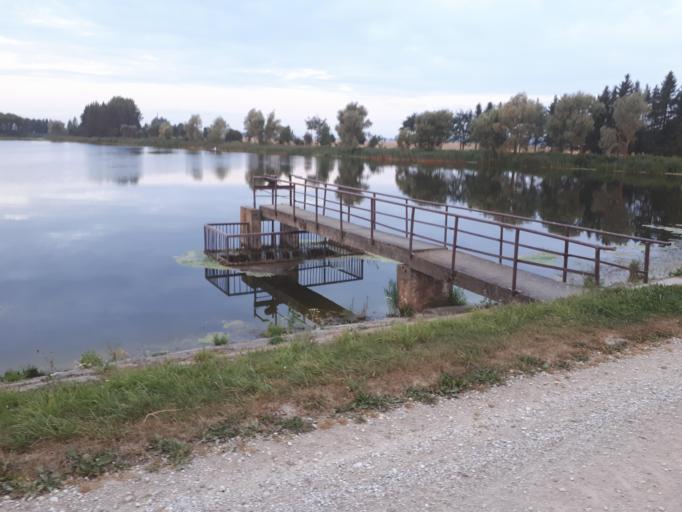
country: LT
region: Siauliu apskritis
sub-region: Joniskis
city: Joniskis
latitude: 56.1820
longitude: 23.6863
